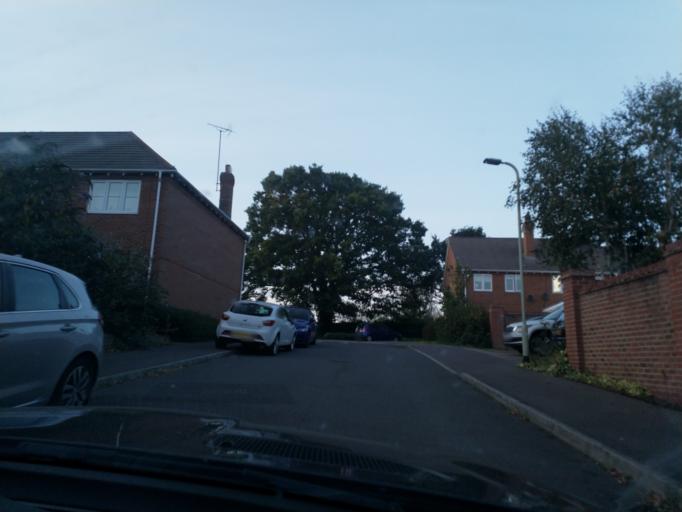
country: GB
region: England
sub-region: Kent
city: Leysdown-on-Sea
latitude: 51.4387
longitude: 0.9037
